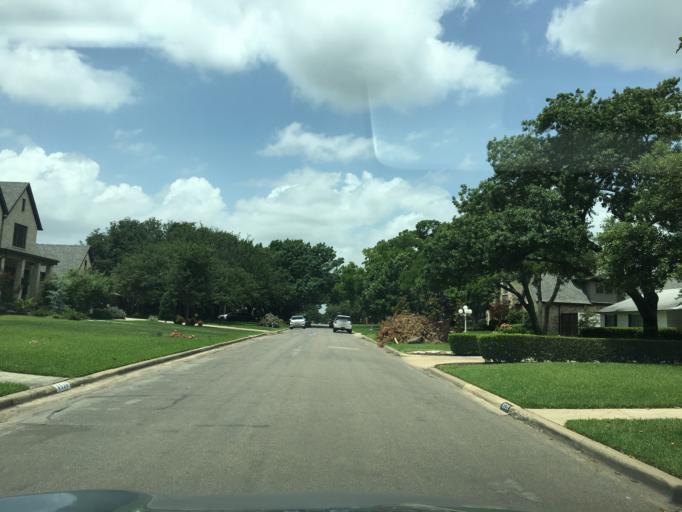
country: US
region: Texas
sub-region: Dallas County
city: University Park
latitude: 32.8926
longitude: -96.7914
